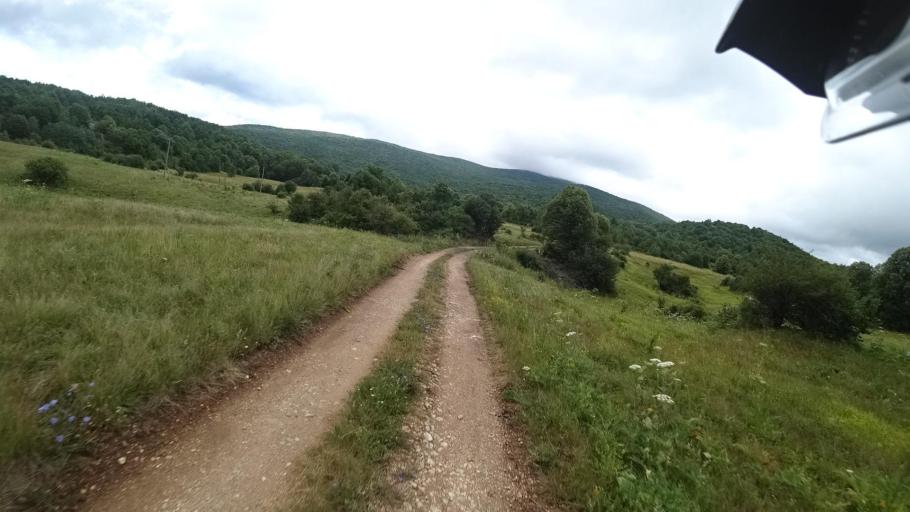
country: HR
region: Licko-Senjska
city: Jezerce
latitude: 44.7744
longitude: 15.4865
